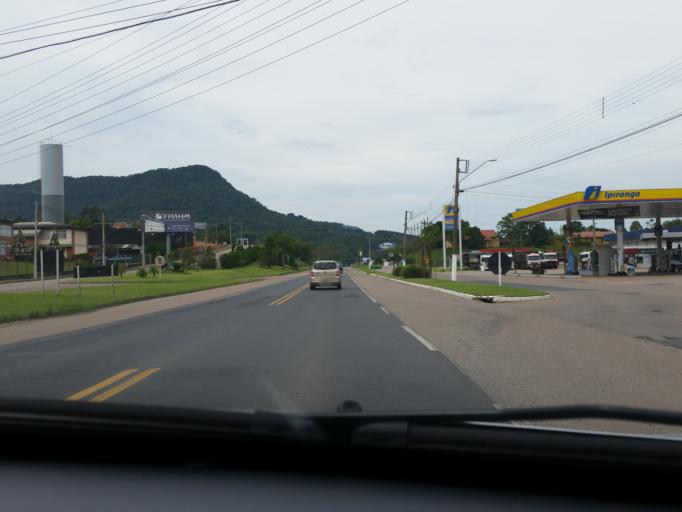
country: BR
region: Santa Catarina
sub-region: Rio Do Sul
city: Rio do Sul
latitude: -27.1972
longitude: -49.6279
